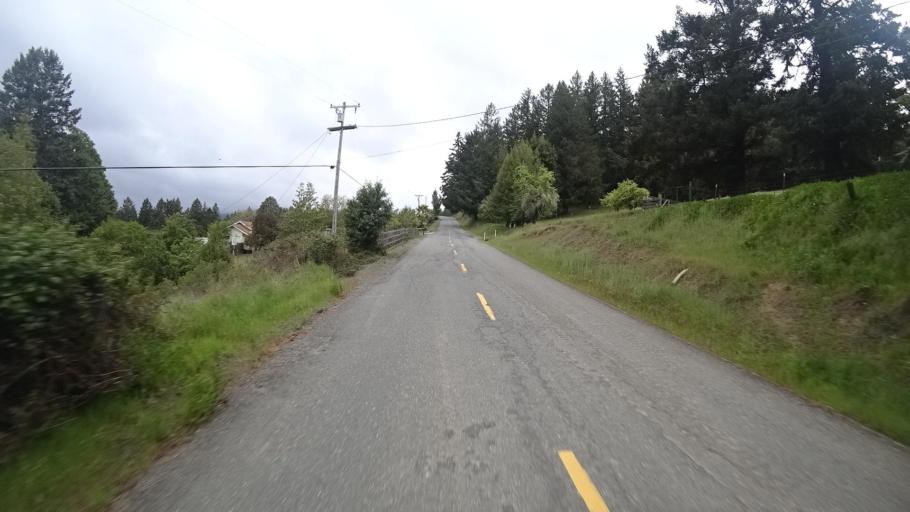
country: US
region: California
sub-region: Humboldt County
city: Redway
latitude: 40.2854
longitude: -123.7997
